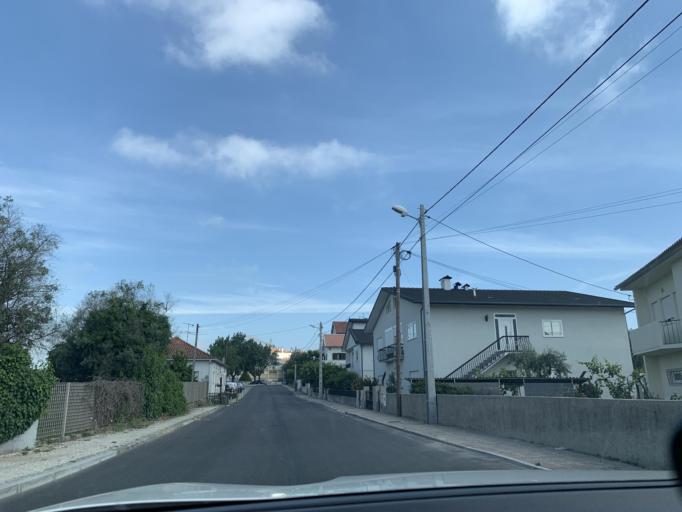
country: PT
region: Viseu
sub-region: Viseu
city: Viseu
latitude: 40.6433
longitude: -7.9180
